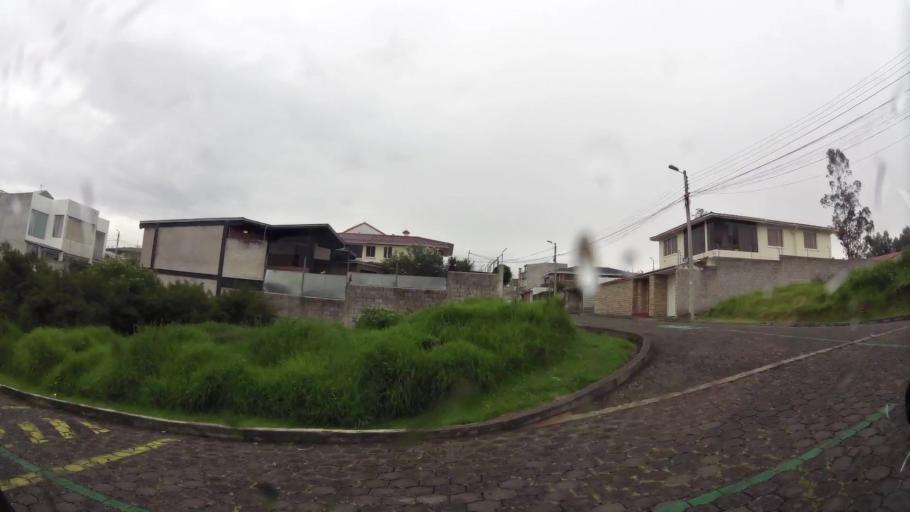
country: EC
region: Pichincha
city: Sangolqui
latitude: -0.3234
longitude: -78.4334
